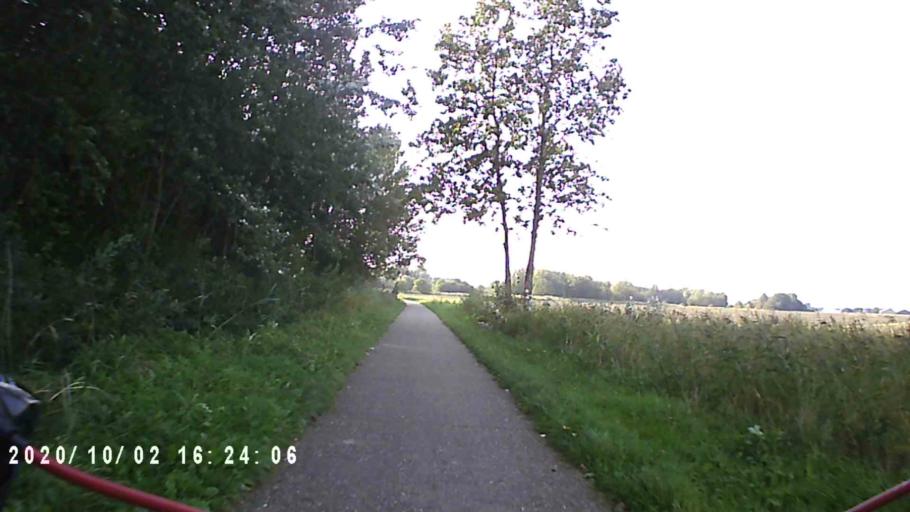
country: NL
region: Groningen
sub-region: Gemeente Zuidhorn
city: Grijpskerk
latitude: 53.2823
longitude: 6.3176
